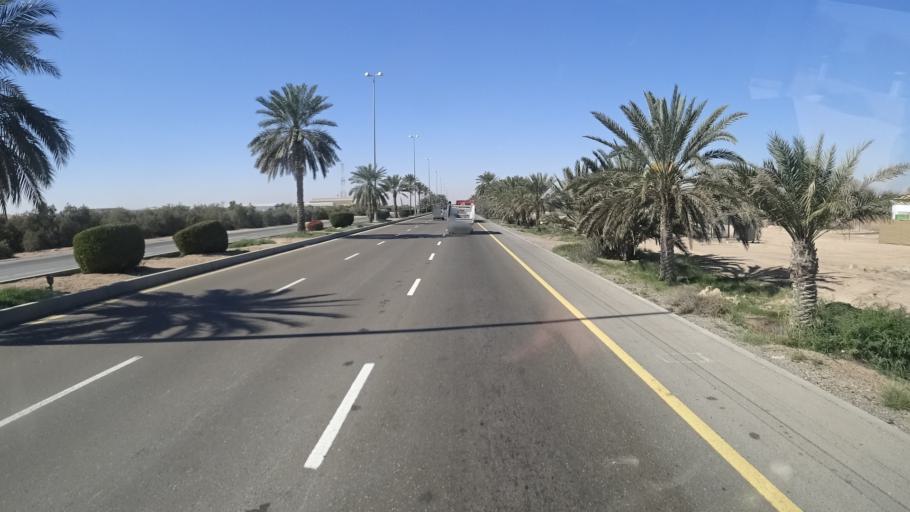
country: AE
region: Abu Dhabi
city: Al Ain
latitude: 24.0817
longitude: 55.6697
